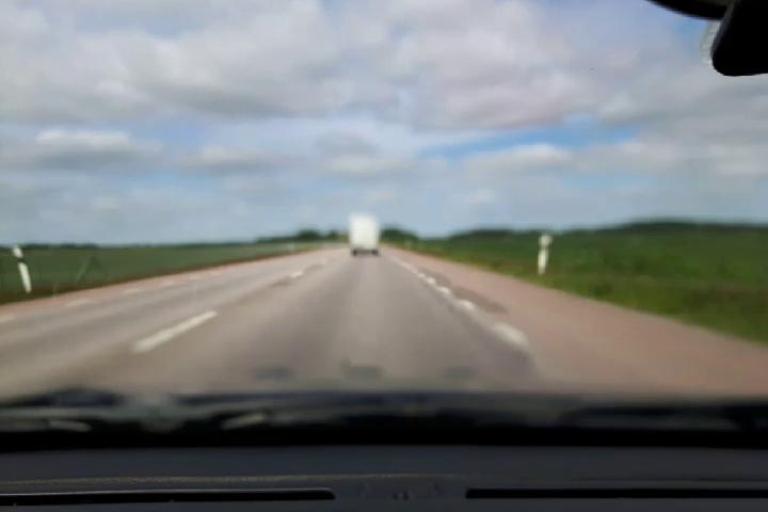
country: SE
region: Uppsala
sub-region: Uppsala Kommun
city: Gamla Uppsala
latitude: 59.8962
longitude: 17.6143
